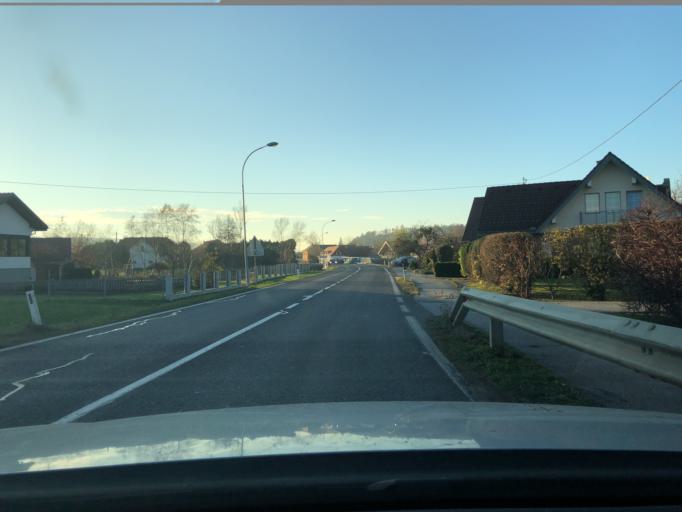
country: AT
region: Styria
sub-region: Politischer Bezirk Hartberg-Fuerstenfeld
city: Nestelbach im Ilztal
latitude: 47.0982
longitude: 15.8526
